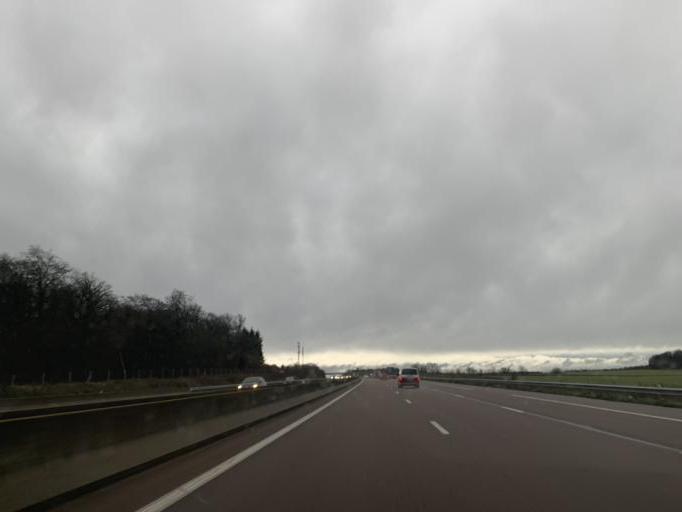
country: FR
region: Bourgogne
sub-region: Departement de la Cote-d'Or
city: Selongey
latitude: 47.6375
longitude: 5.1804
